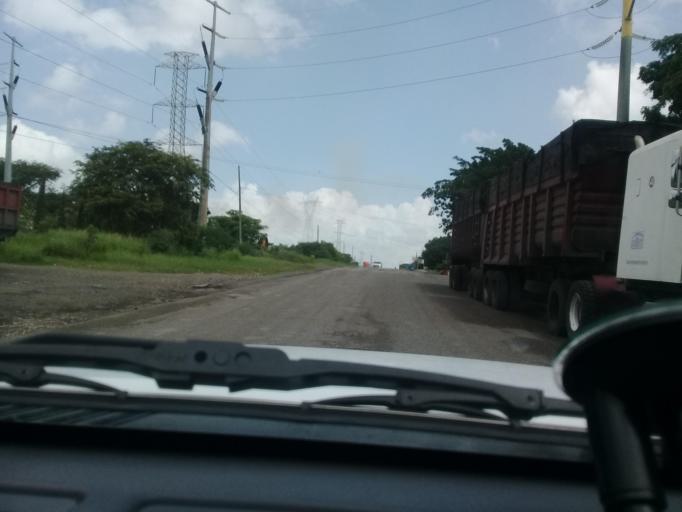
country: MX
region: Veracruz
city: Moralillo
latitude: 22.2185
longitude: -98.0019
